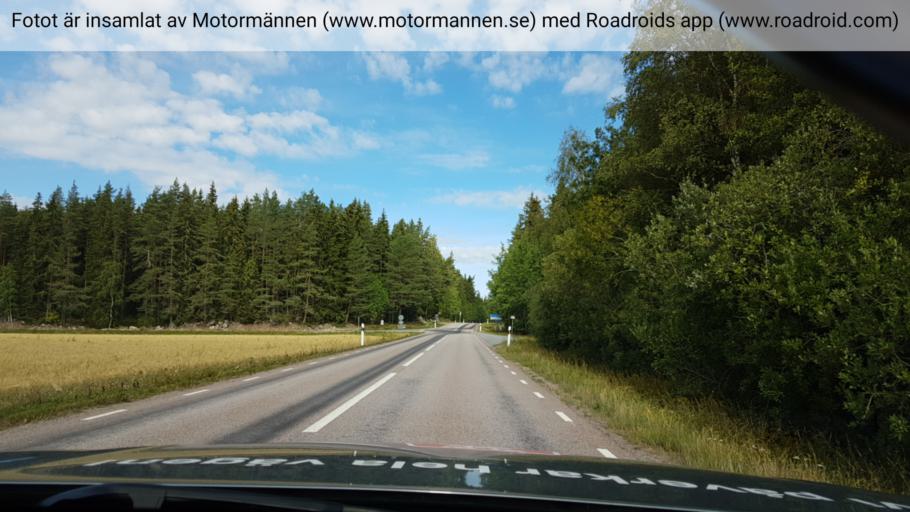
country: SE
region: Uppsala
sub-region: Heby Kommun
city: OEstervala
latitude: 60.0000
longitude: 17.3074
